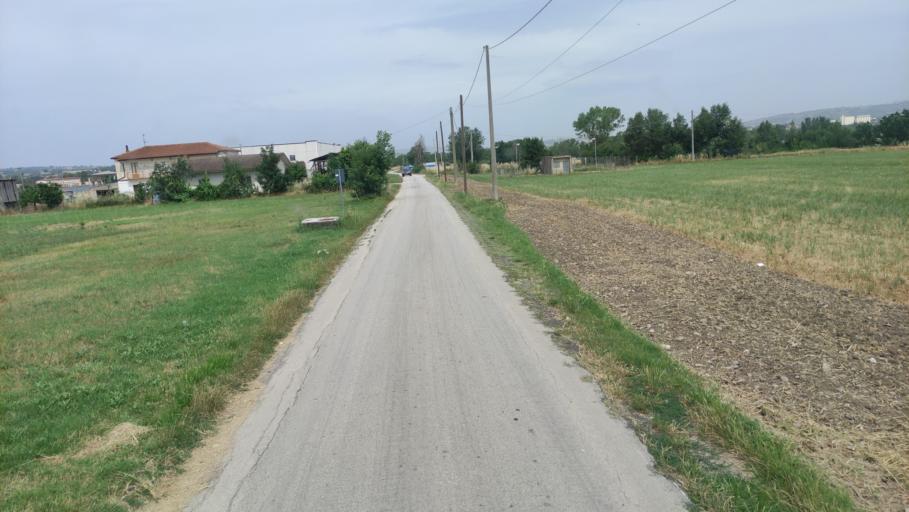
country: IT
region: Campania
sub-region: Provincia di Avellino
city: Sturno
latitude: 41.0510
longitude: 15.1244
